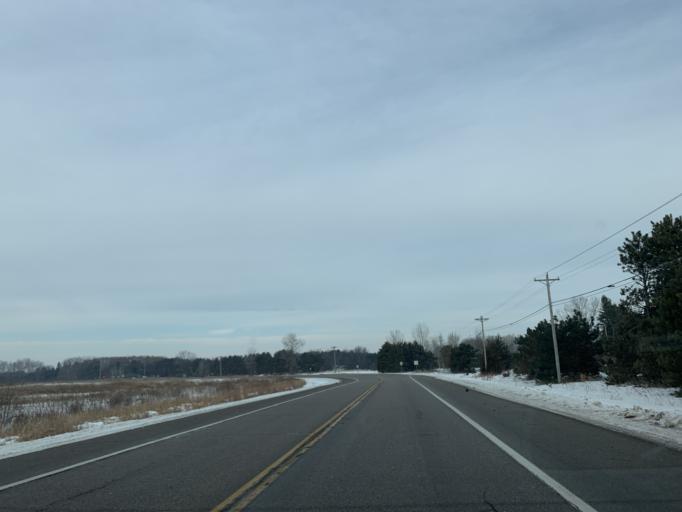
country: US
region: Minnesota
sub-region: Washington County
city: Forest Lake
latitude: 45.2850
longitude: -93.0145
